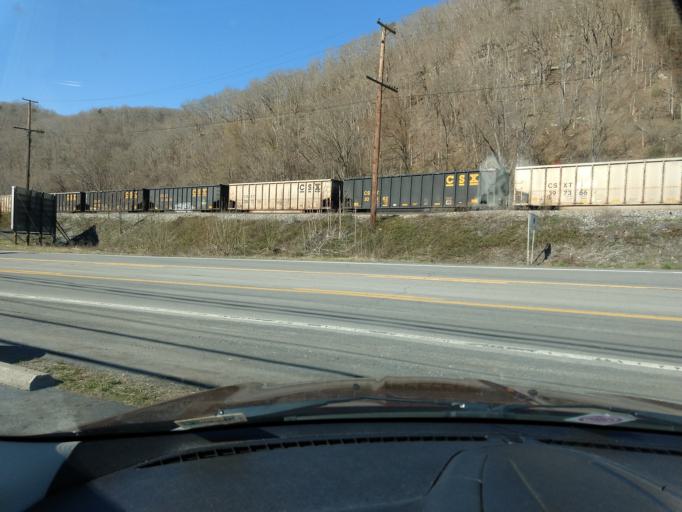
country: US
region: West Virginia
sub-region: Summers County
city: Hinton
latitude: 37.6546
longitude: -80.8846
